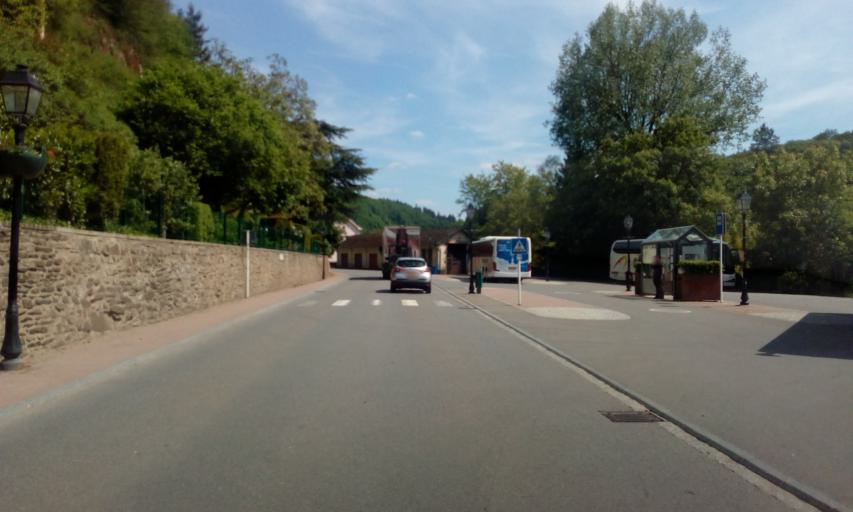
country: LU
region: Diekirch
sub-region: Canton de Vianden
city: Vianden
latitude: 49.9338
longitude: 6.2122
